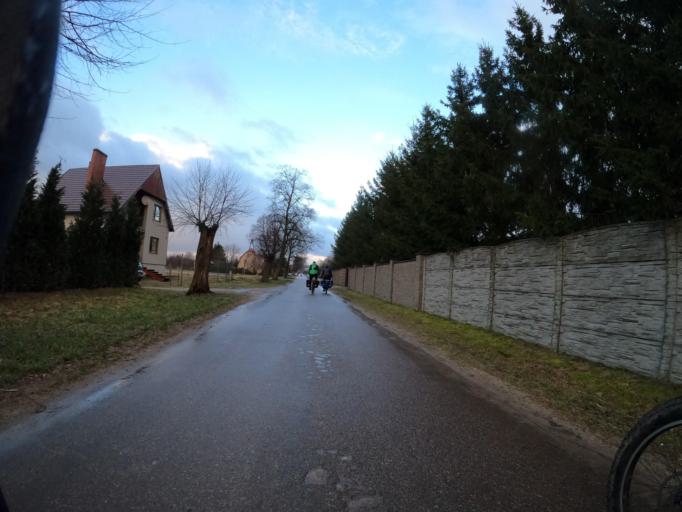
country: PL
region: Greater Poland Voivodeship
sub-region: Powiat zlotowski
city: Sypniewo
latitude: 53.4654
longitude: 16.5984
